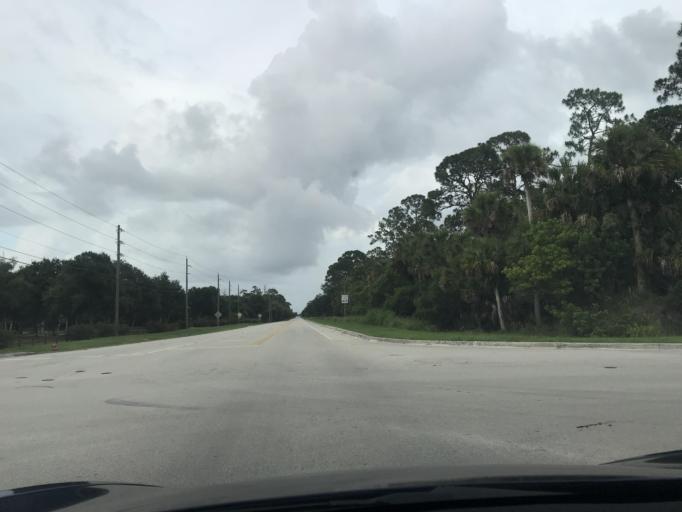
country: US
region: Florida
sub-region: Indian River County
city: West Vero Corridor
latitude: 27.6169
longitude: -80.4635
